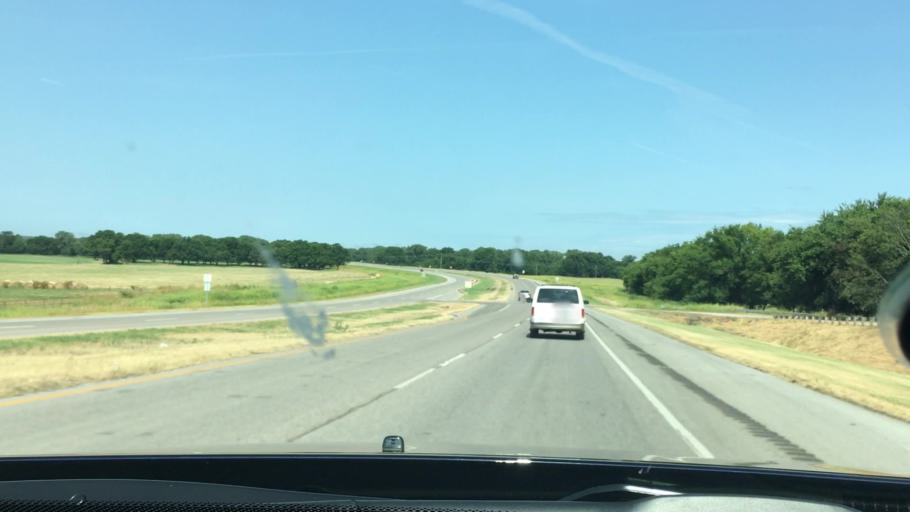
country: US
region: Oklahoma
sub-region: Murray County
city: Davis
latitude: 34.5032
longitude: -97.1296
